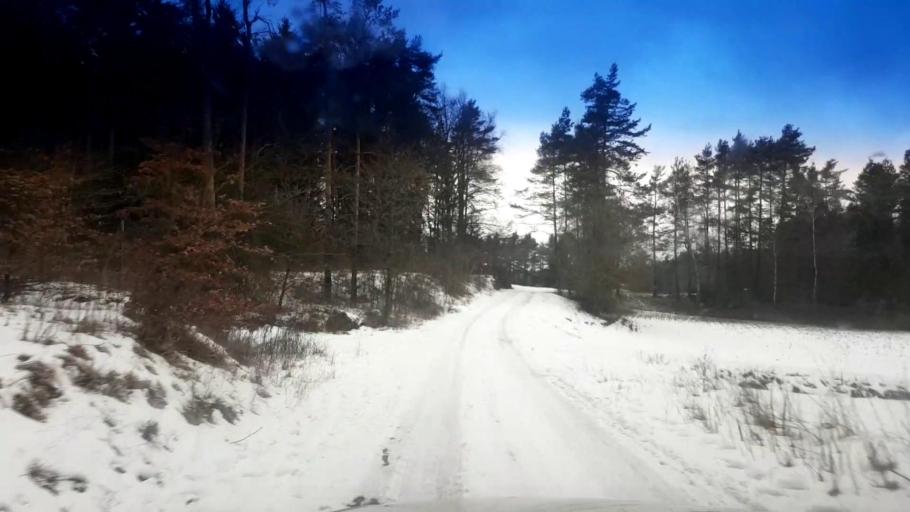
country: DE
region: Bavaria
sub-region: Upper Franconia
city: Wattendorf
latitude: 50.0064
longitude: 11.1253
